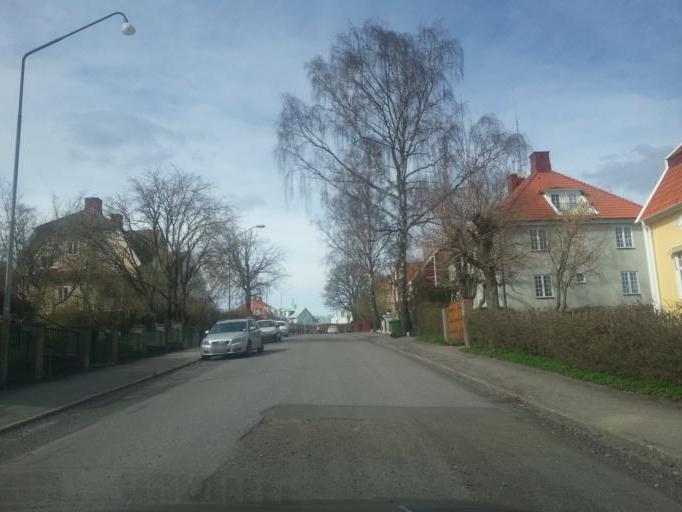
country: SE
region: Joenkoeping
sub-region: Jonkopings Kommun
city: Jonkoping
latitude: 57.7850
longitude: 14.1462
